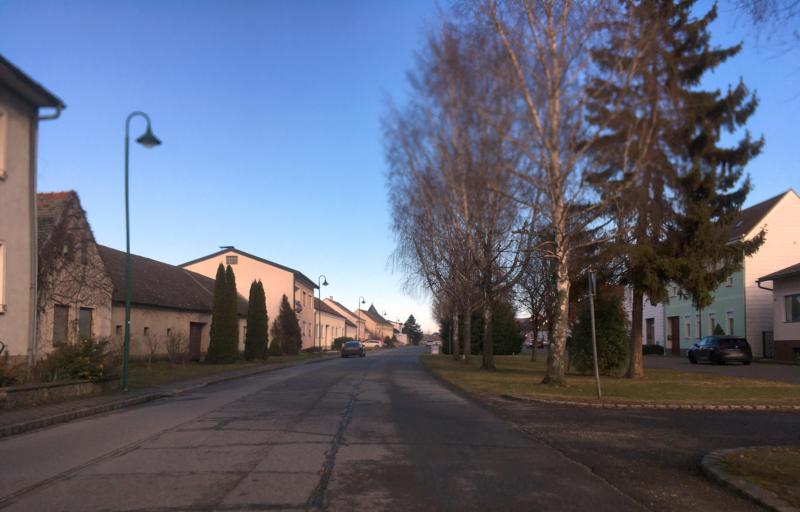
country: AT
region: Lower Austria
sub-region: Politischer Bezirk Bruck an der Leitha
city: Petronell-Carnuntum
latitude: 48.1492
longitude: 16.8348
